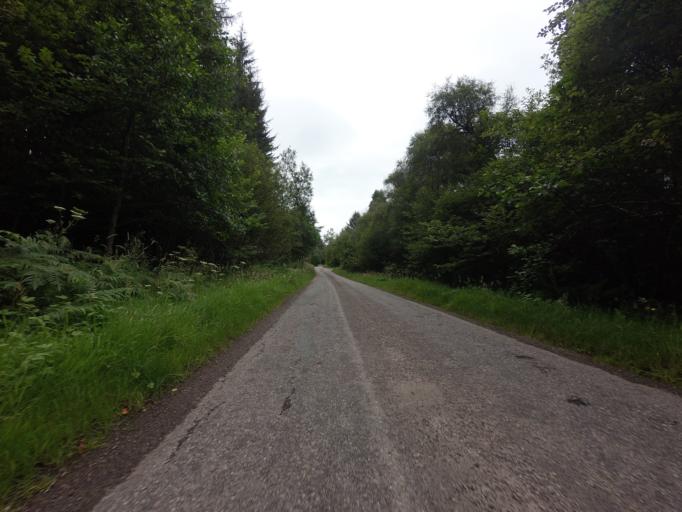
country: GB
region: Scotland
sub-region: Highland
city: Evanton
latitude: 57.9655
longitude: -4.4111
